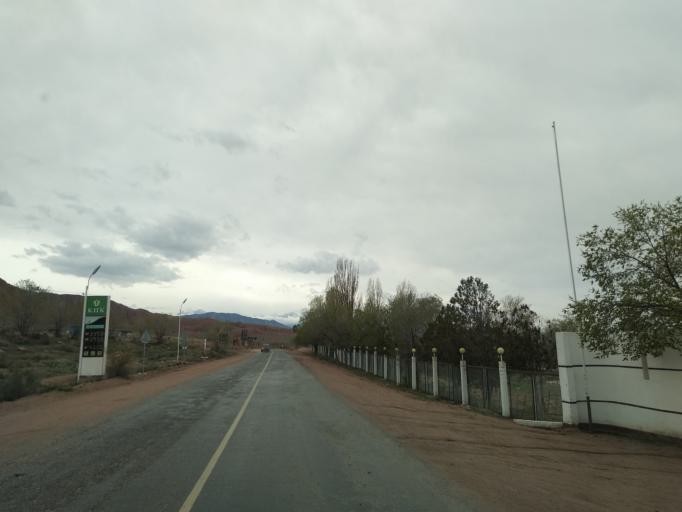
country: KG
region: Ysyk-Koel
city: Kadzhi-Say
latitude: 42.1640
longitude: 77.1647
